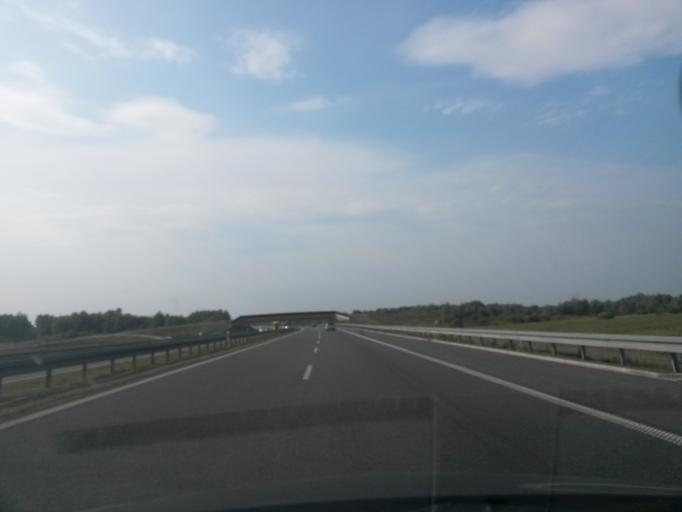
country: PL
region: Lesser Poland Voivodeship
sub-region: Powiat bochenski
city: Jodlowka
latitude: 50.0045
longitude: 20.5434
